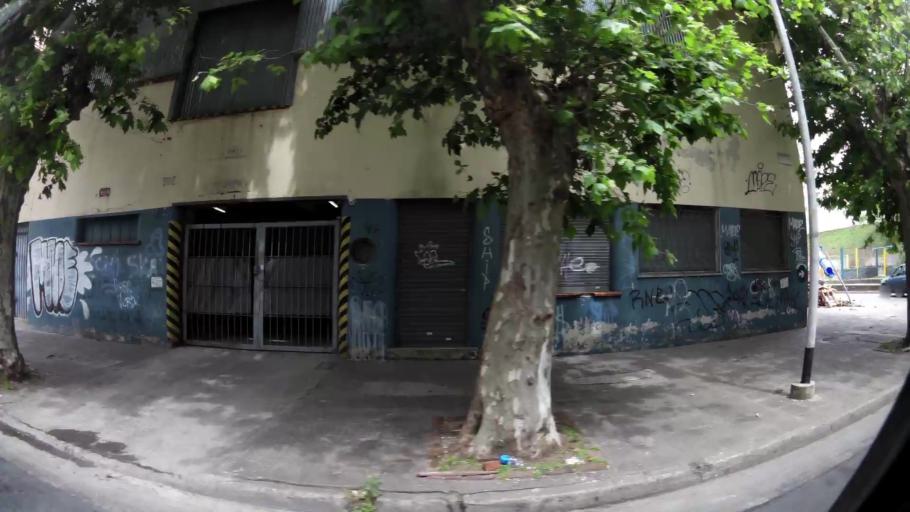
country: AR
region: Buenos Aires
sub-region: Partido de Avellaneda
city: Avellaneda
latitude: -34.6681
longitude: -58.3607
